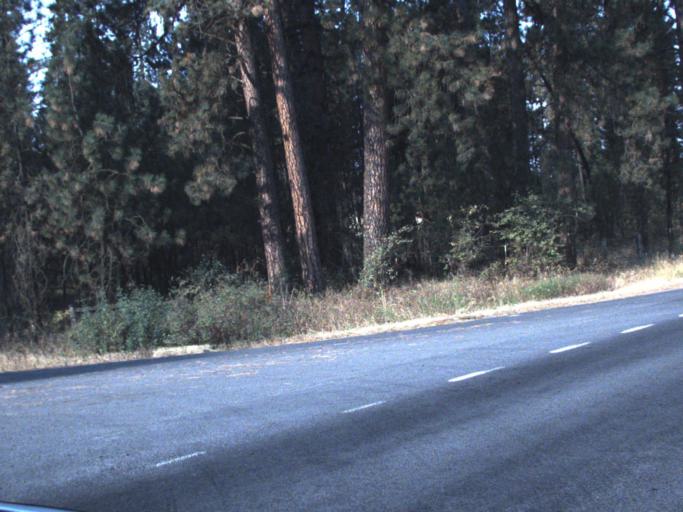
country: US
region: Washington
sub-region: Spokane County
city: Veradale
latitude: 47.4410
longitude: -117.1054
